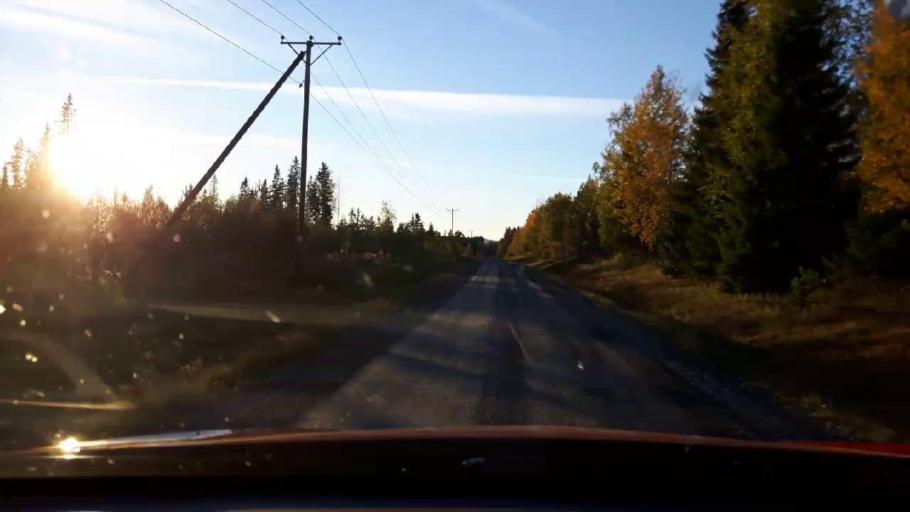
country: SE
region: Jaemtland
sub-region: Krokoms Kommun
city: Krokom
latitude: 63.4293
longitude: 14.4447
